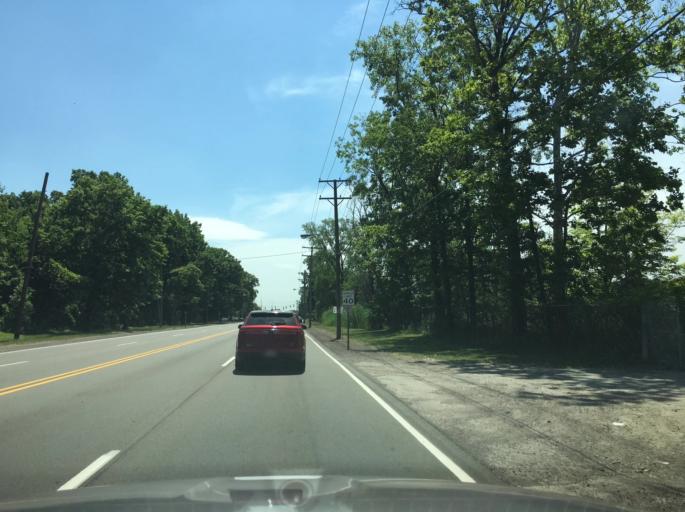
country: US
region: Michigan
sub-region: Wayne County
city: Melvindale
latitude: 42.2890
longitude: -83.2049
